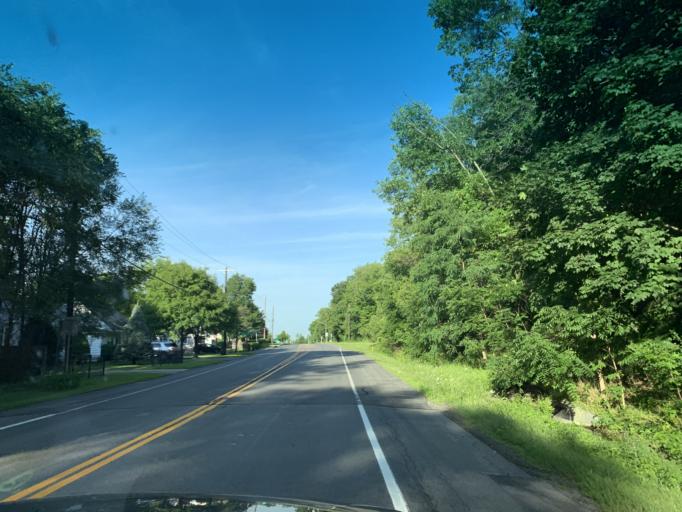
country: US
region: New York
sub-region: Oneida County
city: New Hartford
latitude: 43.0758
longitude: -75.3148
